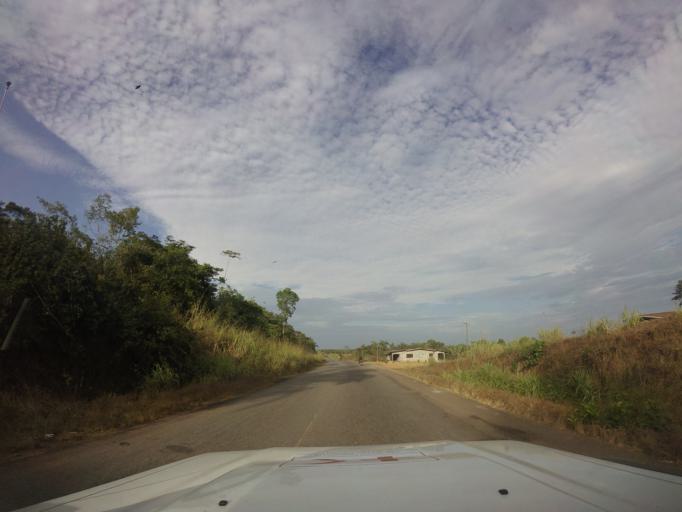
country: LR
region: Bomi
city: Tubmanburg
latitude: 6.7174
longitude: -11.0620
